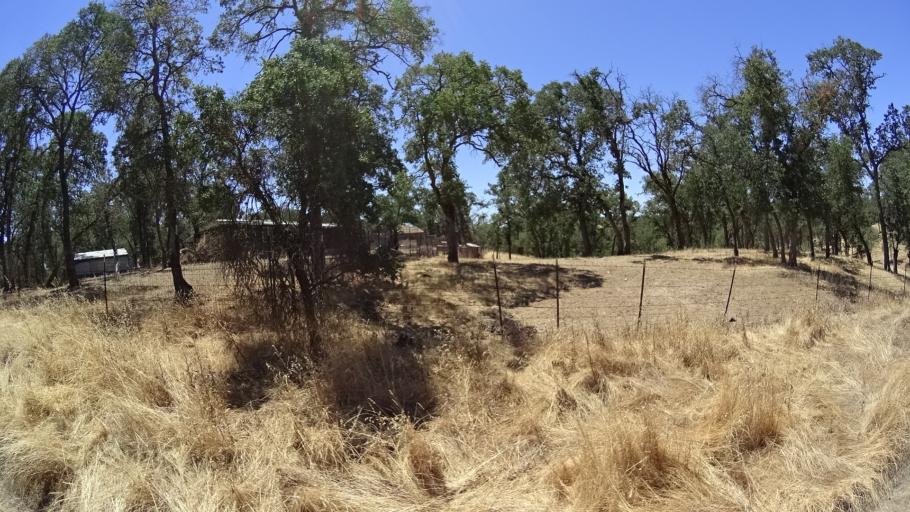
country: US
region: California
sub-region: Calaveras County
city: Copperopolis
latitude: 37.9857
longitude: -120.6885
